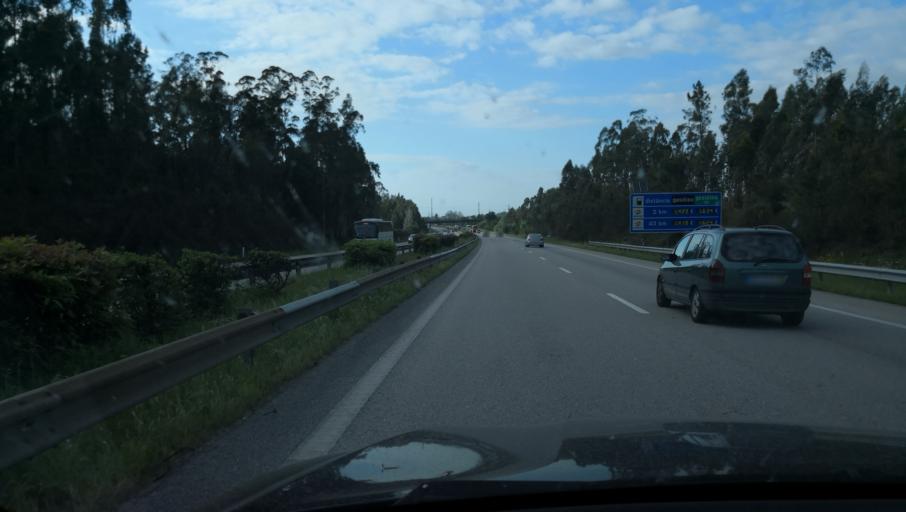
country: PT
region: Aveiro
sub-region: Estarreja
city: Salreu
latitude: 40.7385
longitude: -8.5250
